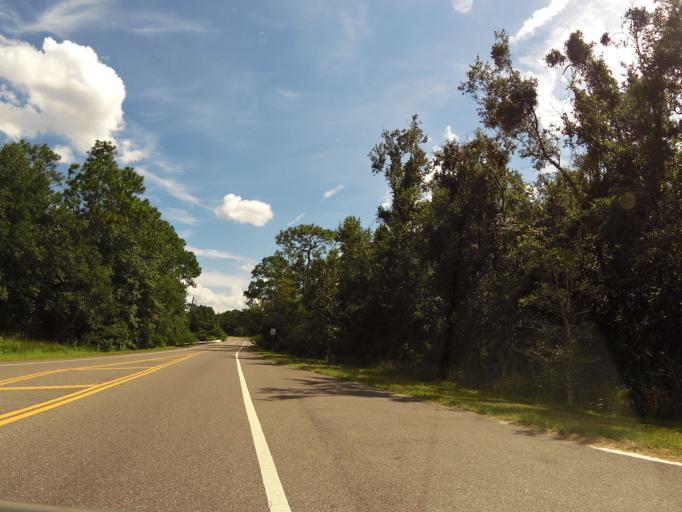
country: US
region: Florida
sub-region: Duval County
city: Jacksonville
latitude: 30.4305
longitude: -81.5803
